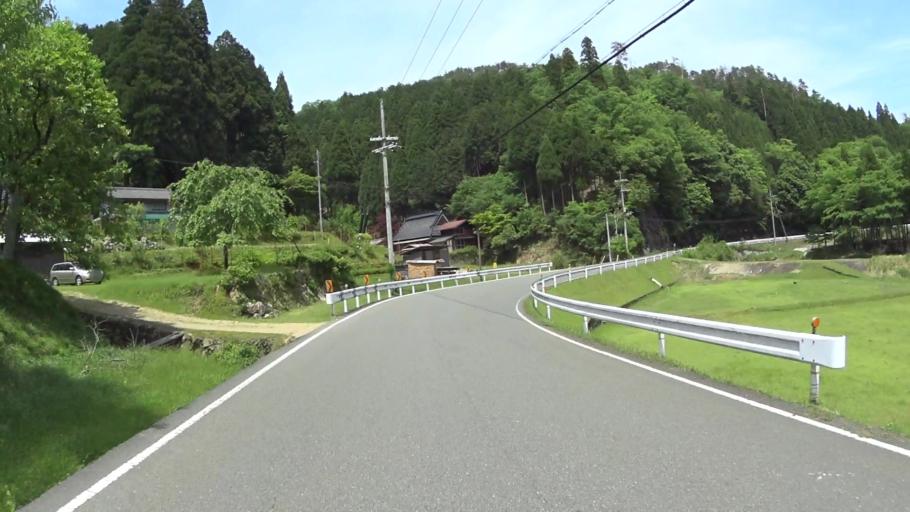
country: JP
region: Kyoto
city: Maizuru
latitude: 35.4175
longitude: 135.4636
